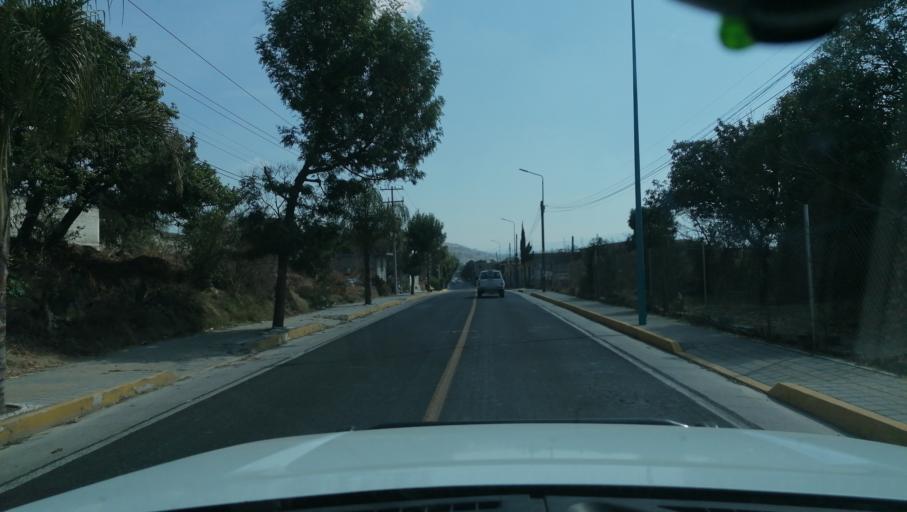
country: MX
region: Tlaxcala
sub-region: Tetlatlahuca
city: Santa Cruz Aquiahuac
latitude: 19.2382
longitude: -98.2727
